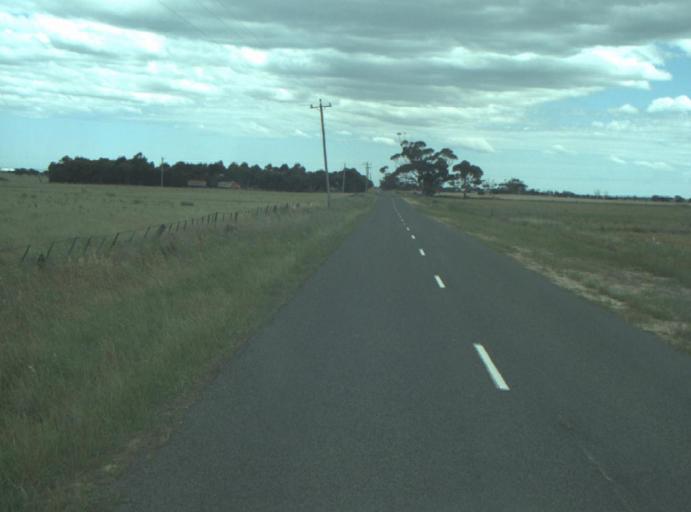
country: AU
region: Victoria
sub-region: Wyndham
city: Little River
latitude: -37.9538
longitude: 144.4646
